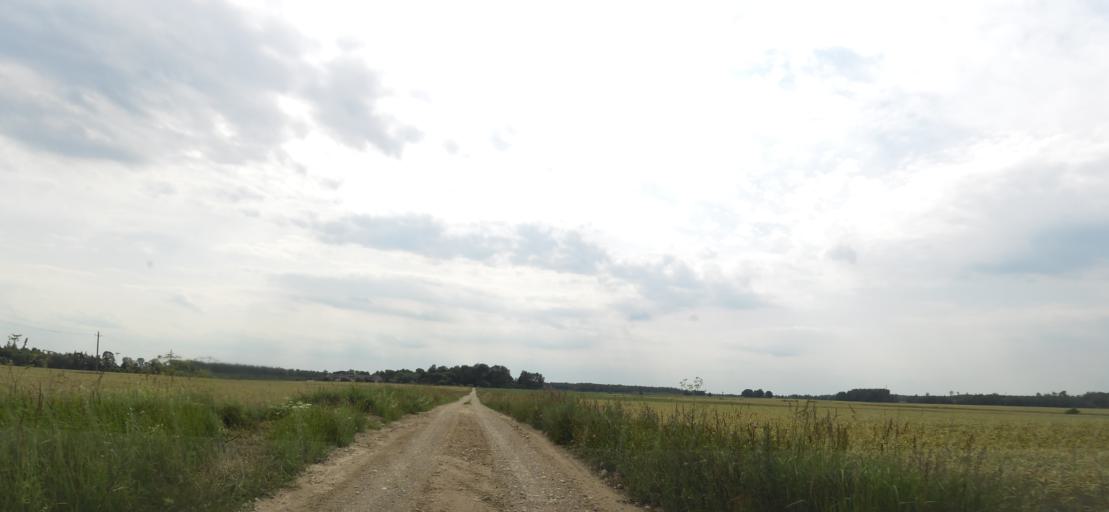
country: LT
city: Obeliai
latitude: 56.1864
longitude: 25.0551
